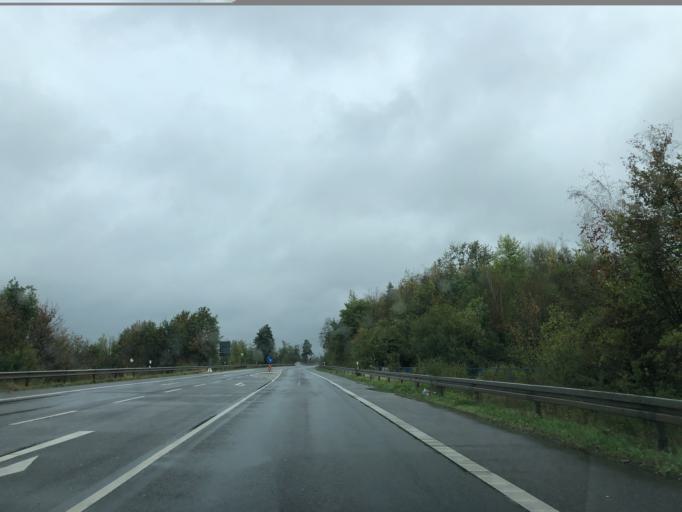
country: DE
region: North Rhine-Westphalia
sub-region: Regierungsbezirk Dusseldorf
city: Grevenbroich
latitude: 51.0800
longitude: 6.5562
